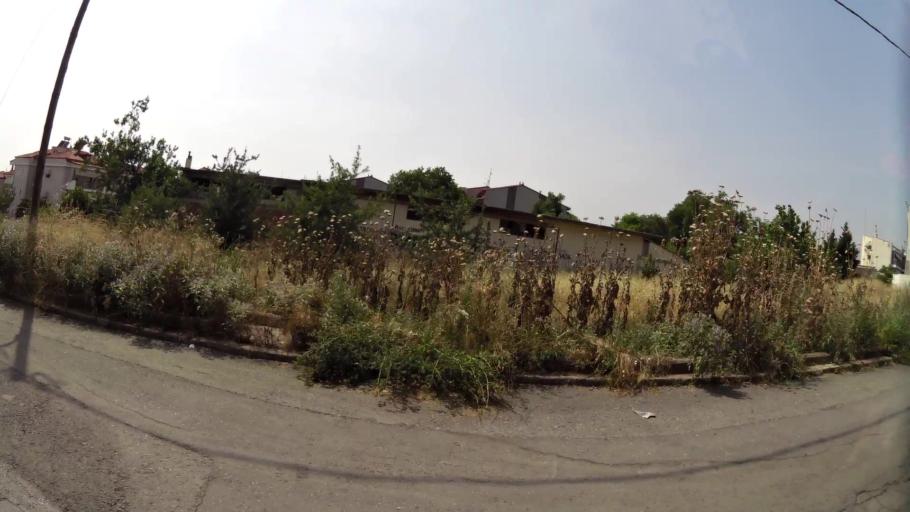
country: GR
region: Central Macedonia
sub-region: Nomos Thessalonikis
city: Efkarpia
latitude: 40.6874
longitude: 22.9503
